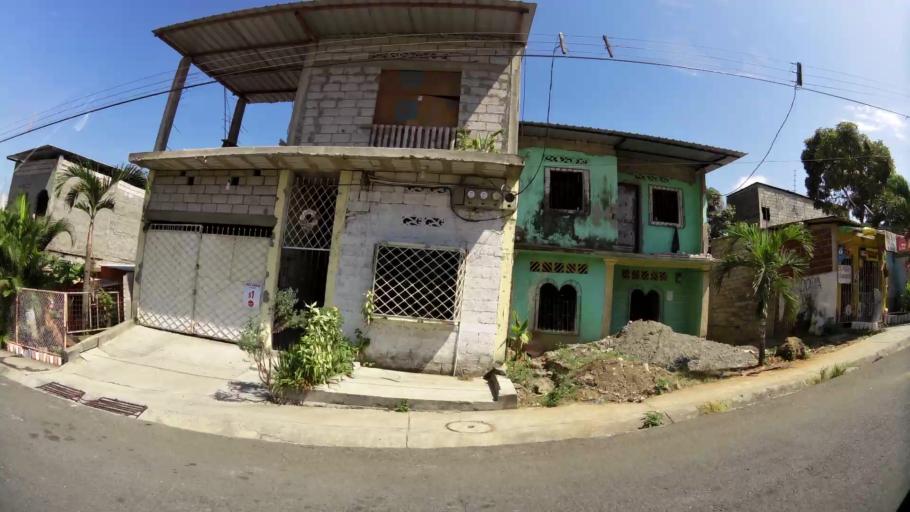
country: EC
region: Guayas
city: Guayaquil
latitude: -2.1302
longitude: -79.9214
